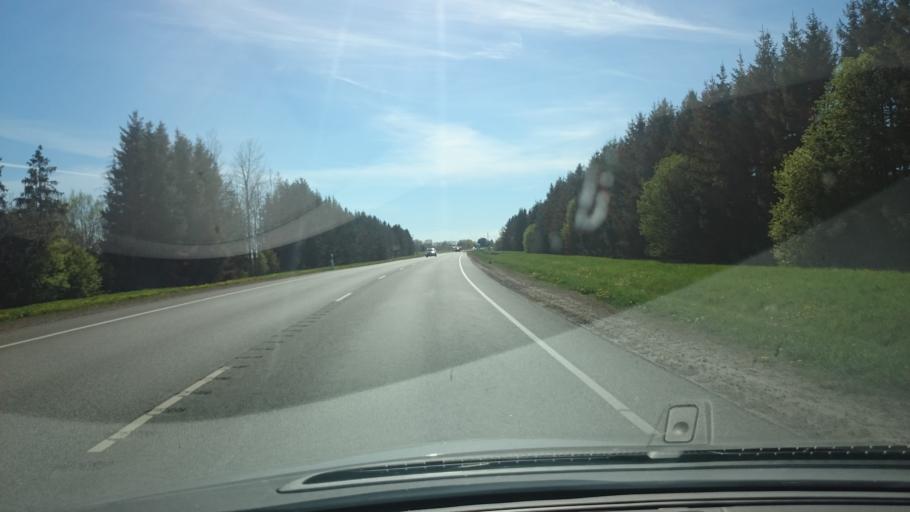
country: EE
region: Ida-Virumaa
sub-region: Kohtla-Nomme vald
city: Kohtla-Nomme
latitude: 59.4126
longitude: 27.1347
